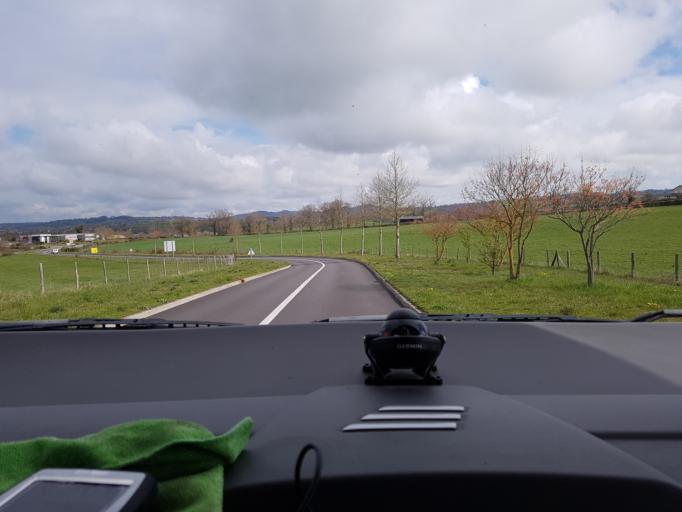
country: FR
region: Midi-Pyrenees
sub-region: Departement de l'Aveyron
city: Colombies
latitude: 44.3992
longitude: 2.3011
